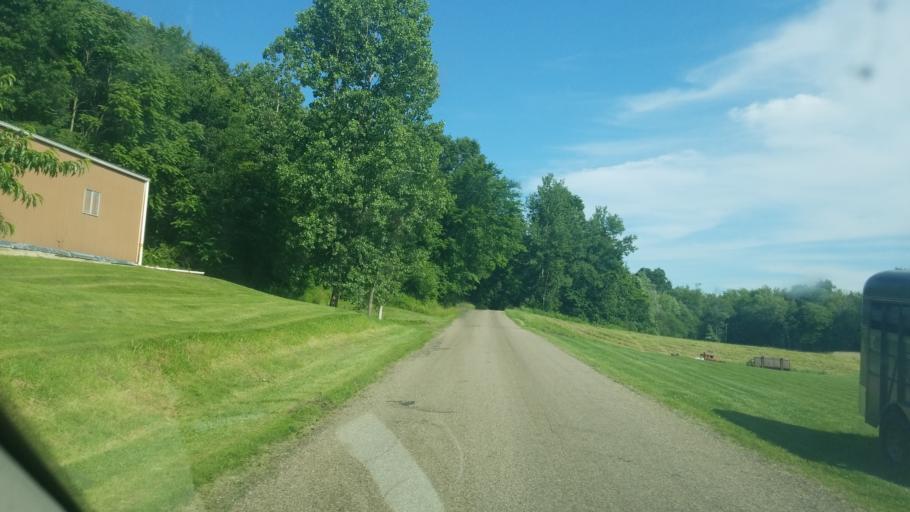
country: US
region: Ohio
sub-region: Holmes County
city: Millersburg
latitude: 40.4253
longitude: -81.9564
